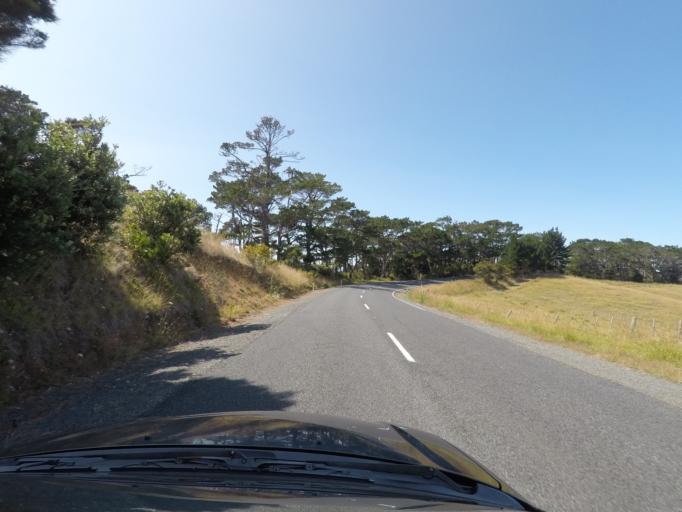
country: NZ
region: Auckland
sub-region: Auckland
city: Warkworth
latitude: -36.4461
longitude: 174.7569
